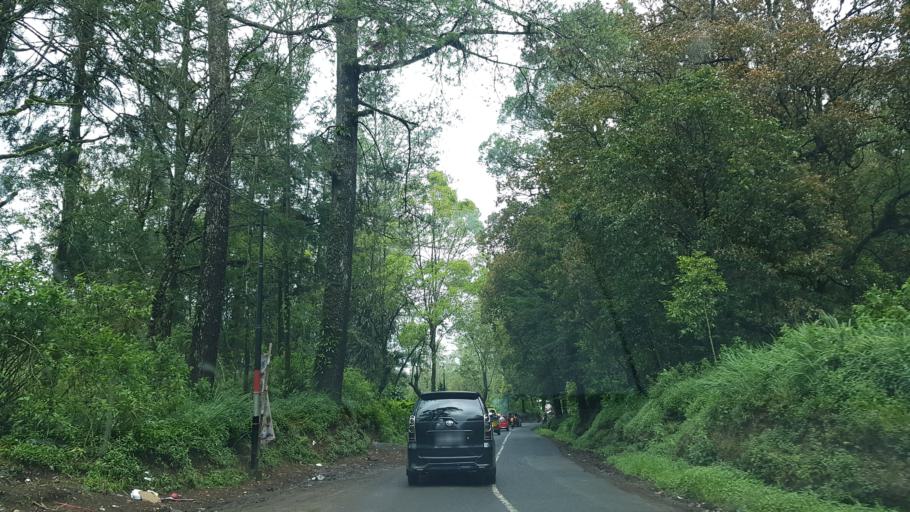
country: ID
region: West Java
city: Banjar
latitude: -7.1431
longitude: 107.3918
